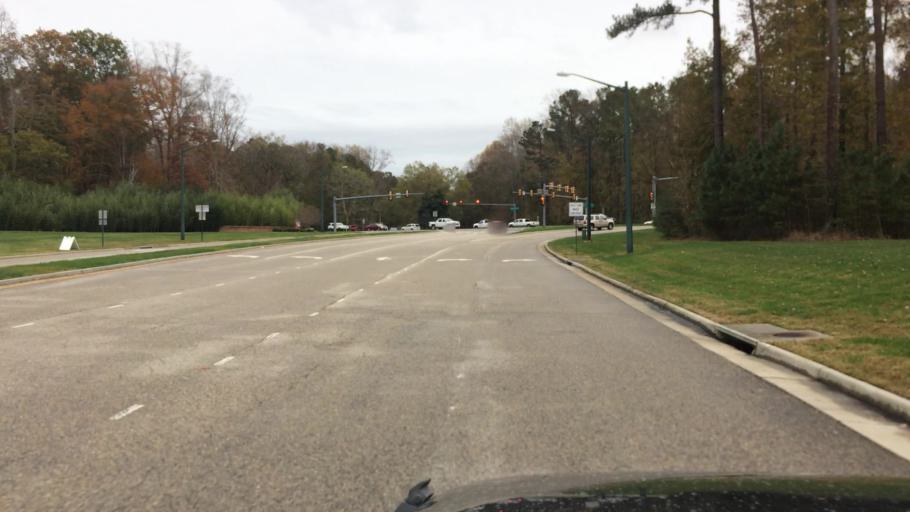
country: US
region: Virginia
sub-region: City of Williamsburg
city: Williamsburg
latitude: 37.2483
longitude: -76.6837
